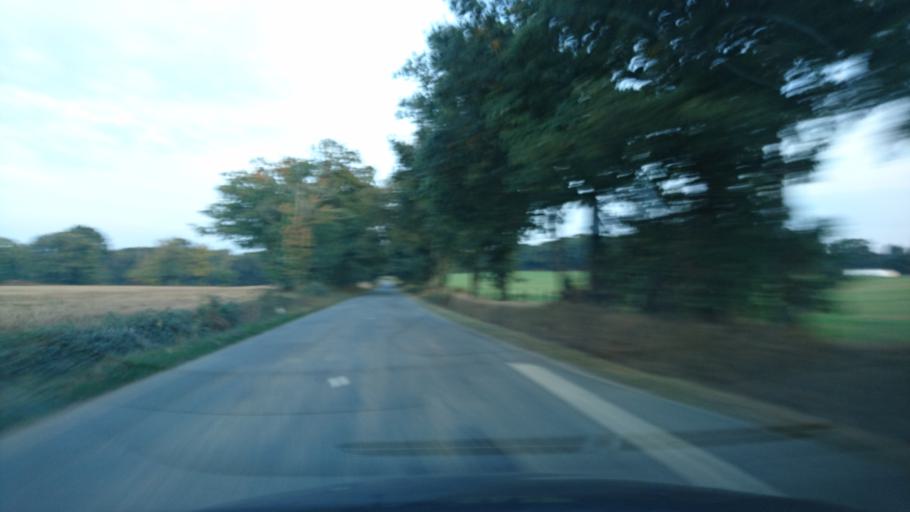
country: FR
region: Brittany
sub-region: Departement d'Ille-et-Vilaine
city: Maure-de-Bretagne
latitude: 47.8884
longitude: -2.0151
